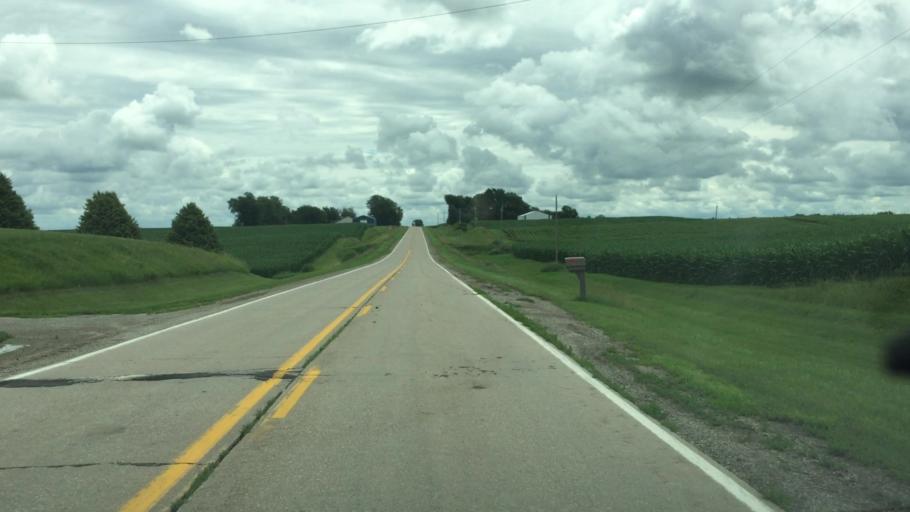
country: US
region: Iowa
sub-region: Jasper County
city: Monroe
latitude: 41.5807
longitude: -93.1183
